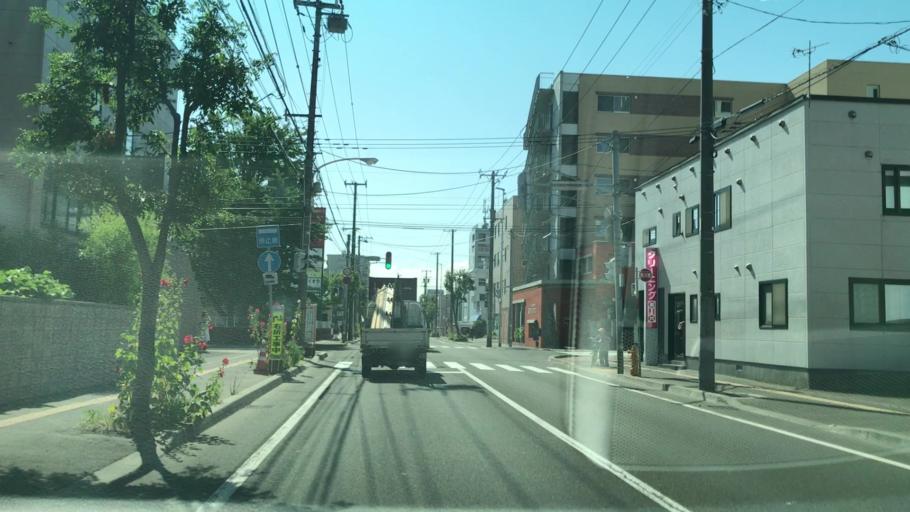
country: JP
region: Hokkaido
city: Sapporo
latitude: 43.0528
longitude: 141.4102
